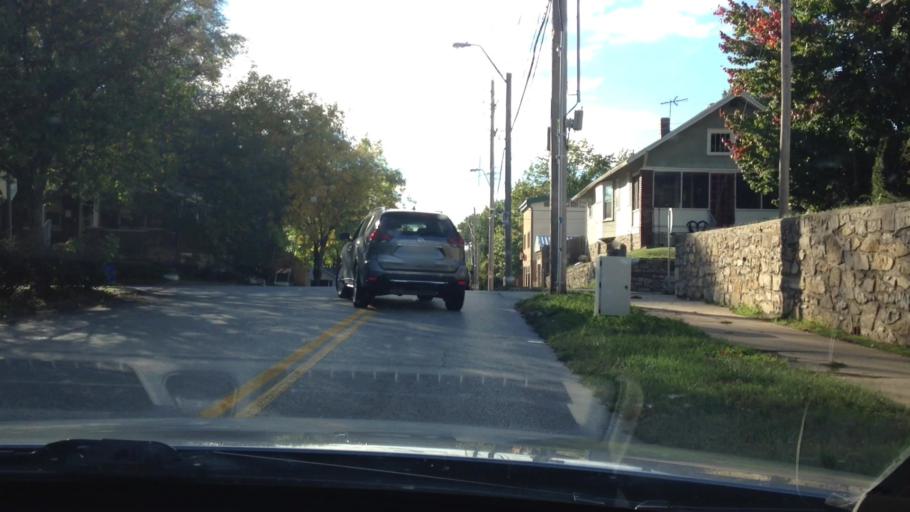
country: US
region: Kansas
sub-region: Johnson County
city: Westwood
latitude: 39.0427
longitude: -94.6023
